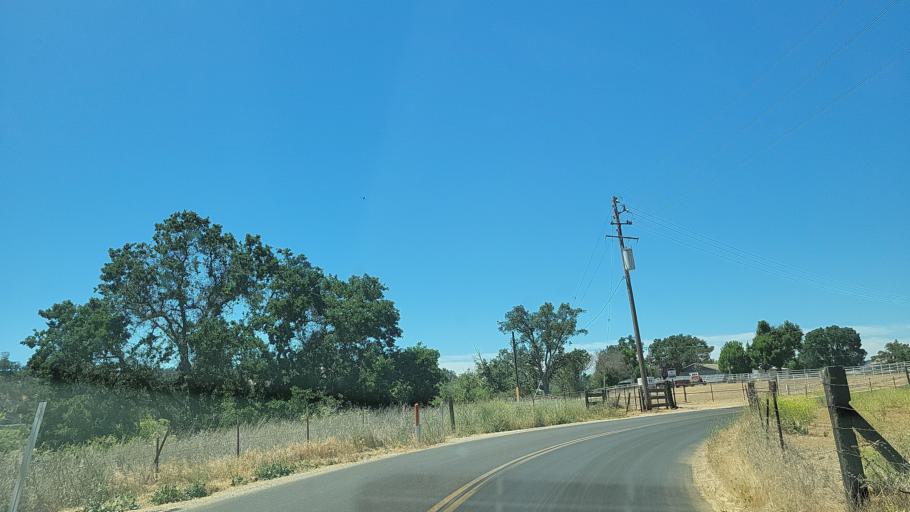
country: US
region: California
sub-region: San Luis Obispo County
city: Atascadero
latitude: 35.4624
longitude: -120.6234
